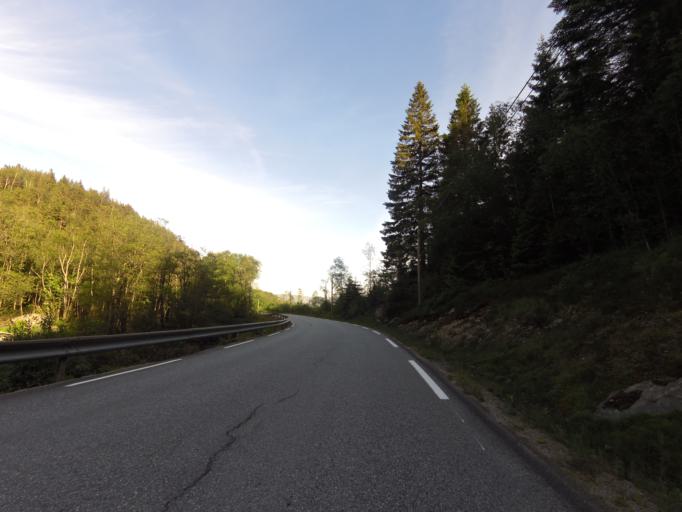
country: NO
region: Vest-Agder
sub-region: Flekkefjord
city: Flekkefjord
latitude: 58.2805
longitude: 6.6240
